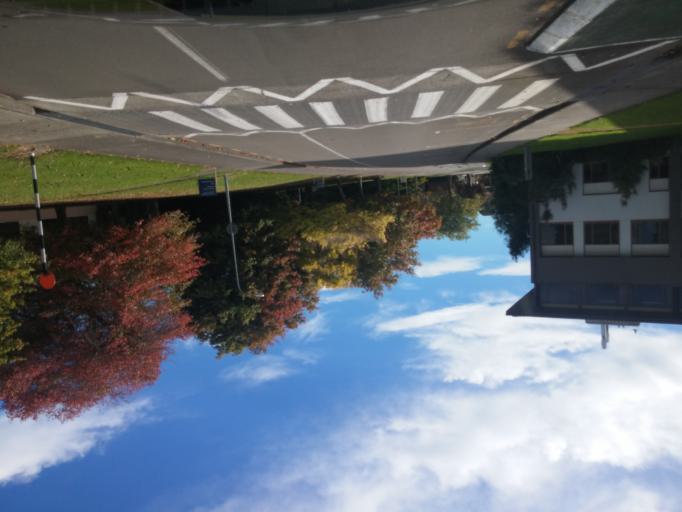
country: NZ
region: Manawatu-Wanganui
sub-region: Palmerston North City
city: Palmerston North
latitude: -40.3888
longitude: 175.6186
